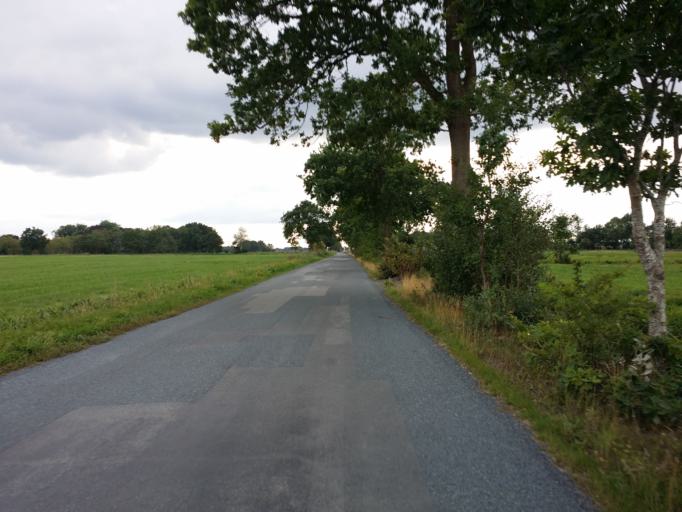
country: DE
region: Lower Saxony
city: Osten
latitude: 53.7394
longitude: 9.2167
